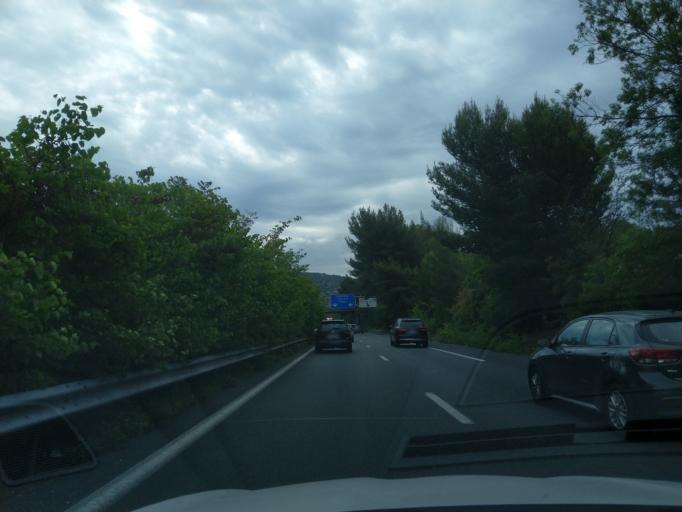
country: FR
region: Provence-Alpes-Cote d'Azur
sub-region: Departement des Bouches-du-Rhone
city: Aubagne
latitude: 43.2849
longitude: 5.5711
